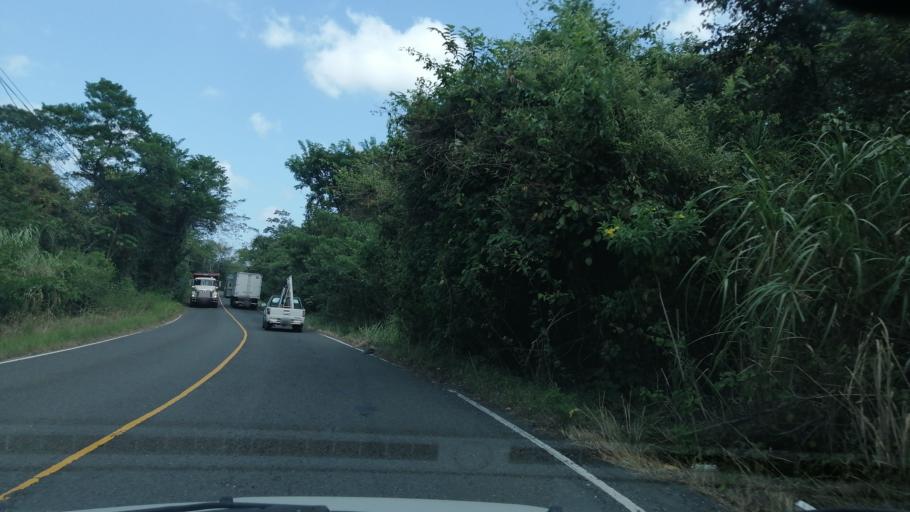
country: PA
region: Panama
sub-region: Distrito de Panama
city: Ancon
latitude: 8.9151
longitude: -79.5668
